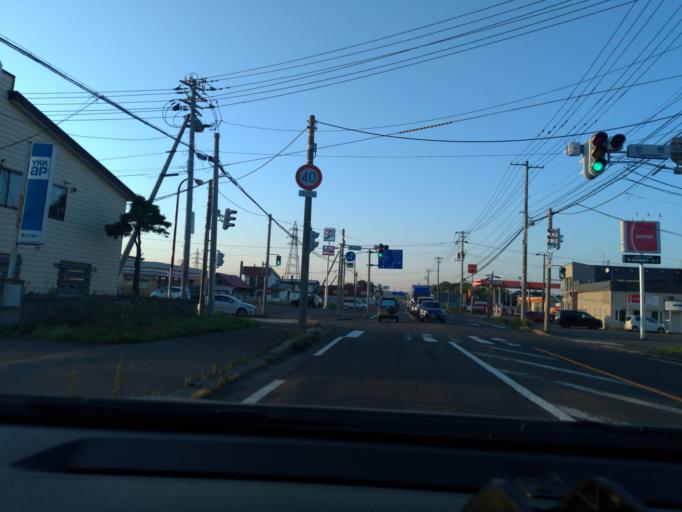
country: JP
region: Hokkaido
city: Tobetsu
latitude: 43.2094
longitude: 141.5189
